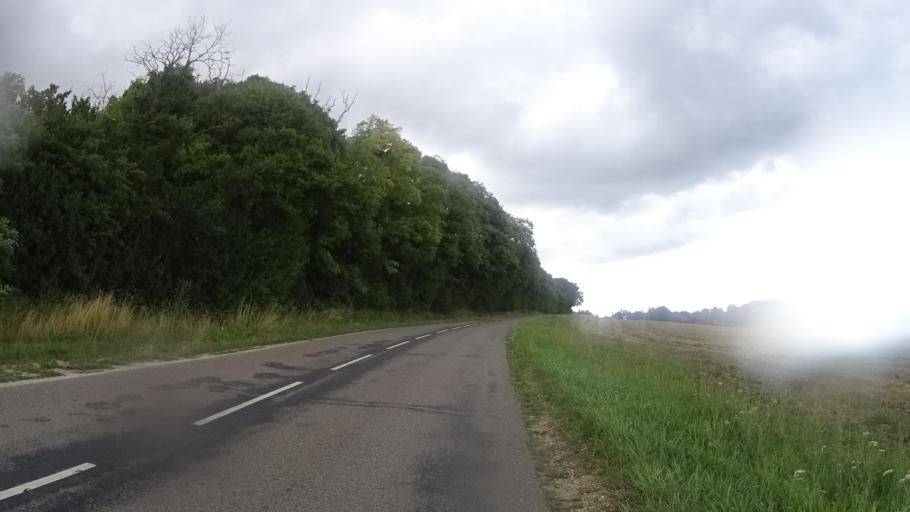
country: FR
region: Champagne-Ardenne
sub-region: Departement de l'Aube
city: Bouilly
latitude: 48.1284
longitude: 4.0118
